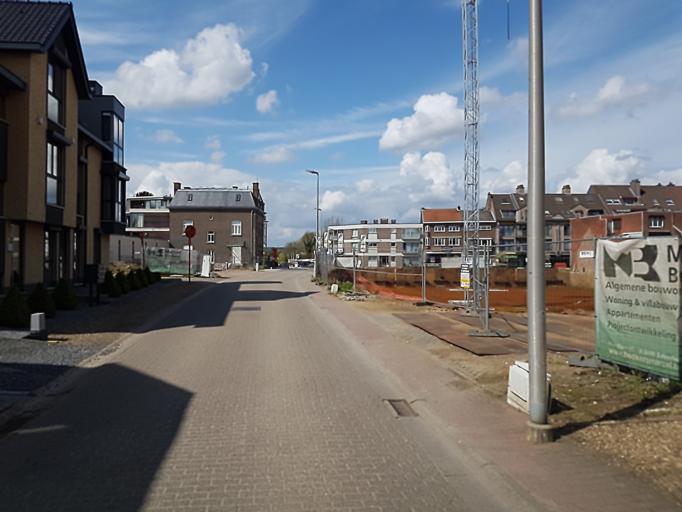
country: BE
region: Flanders
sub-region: Provincie Limburg
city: Lanaken
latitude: 50.8867
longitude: 5.6486
